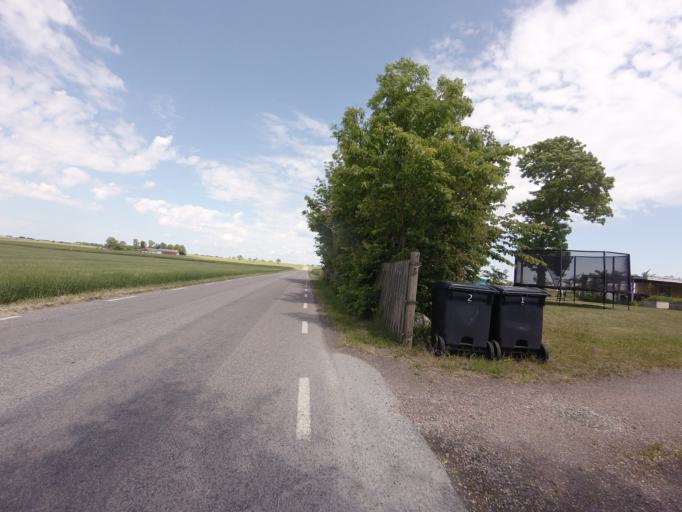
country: SE
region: Skane
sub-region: Trelleborgs Kommun
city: Skare
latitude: 55.4173
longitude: 13.1025
